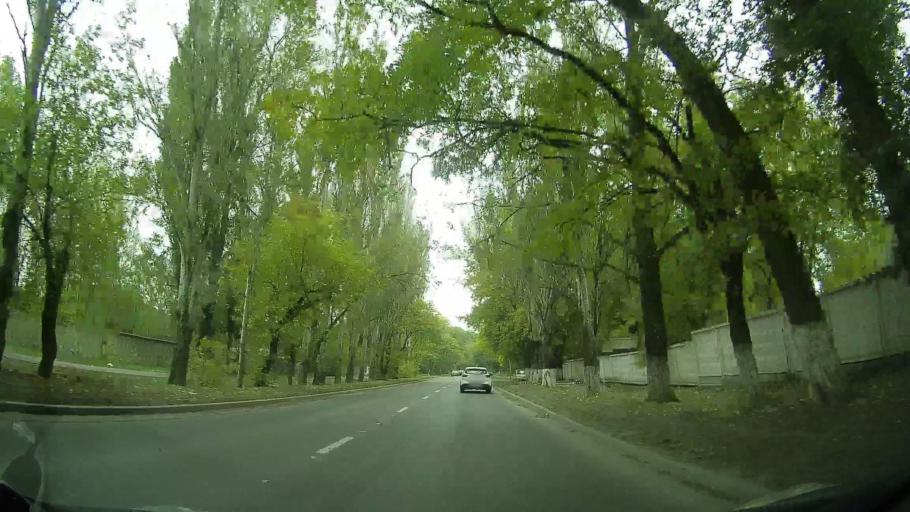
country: RU
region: Rostov
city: Severnyy
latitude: 47.2756
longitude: 39.6642
